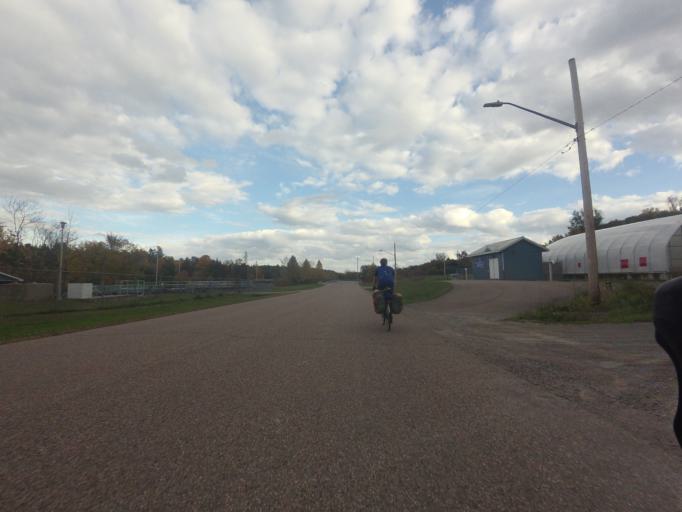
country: CA
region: Ontario
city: Pembroke
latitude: 45.5366
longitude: -77.0960
